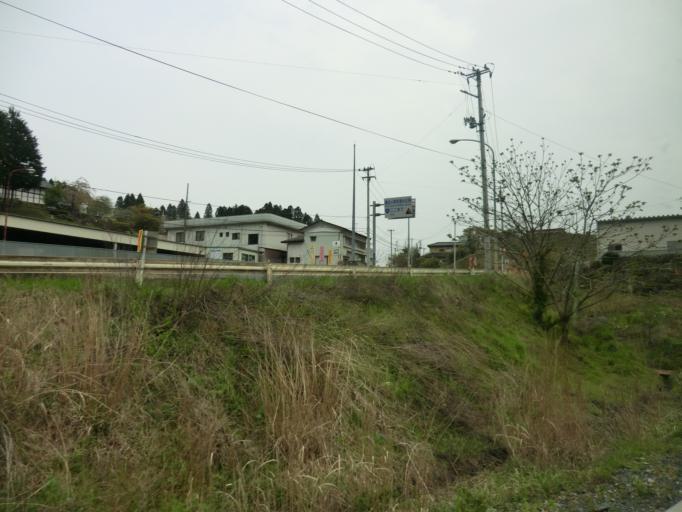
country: JP
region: Miyagi
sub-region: Oshika Gun
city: Onagawa Cho
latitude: 38.7360
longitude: 141.5307
